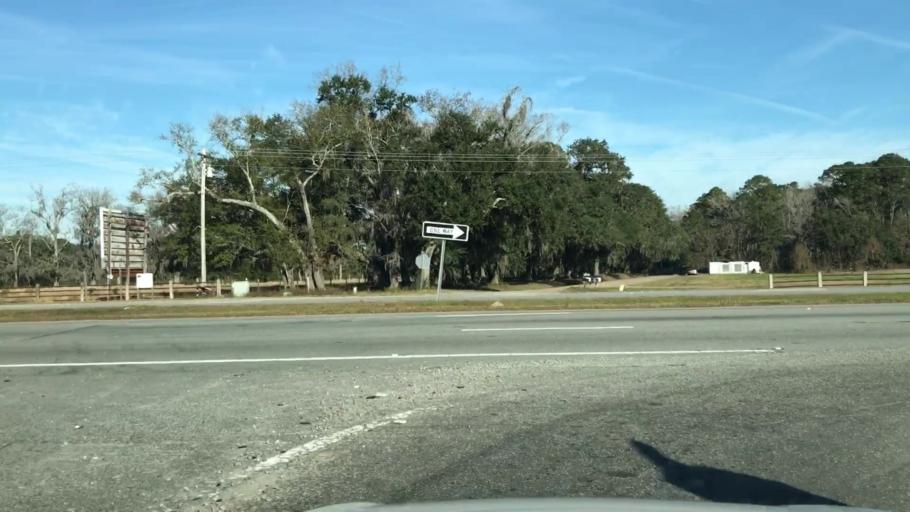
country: US
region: South Carolina
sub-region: Beaufort County
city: Bluffton
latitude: 32.2901
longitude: -80.9211
